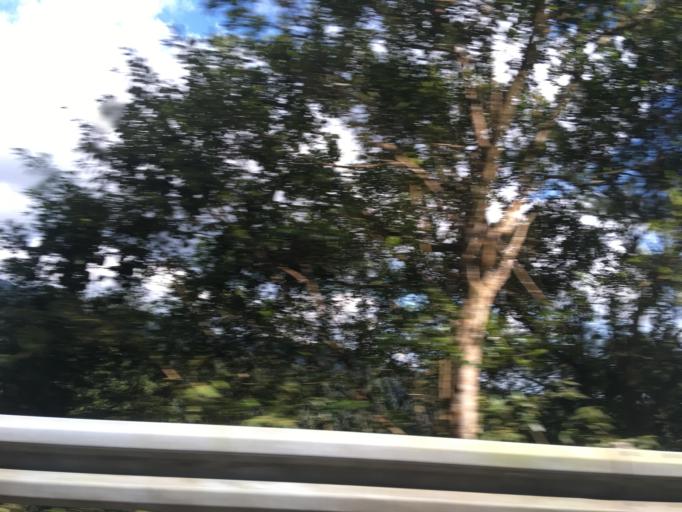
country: TW
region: Taiwan
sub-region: Yilan
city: Yilan
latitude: 24.7517
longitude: 121.6424
